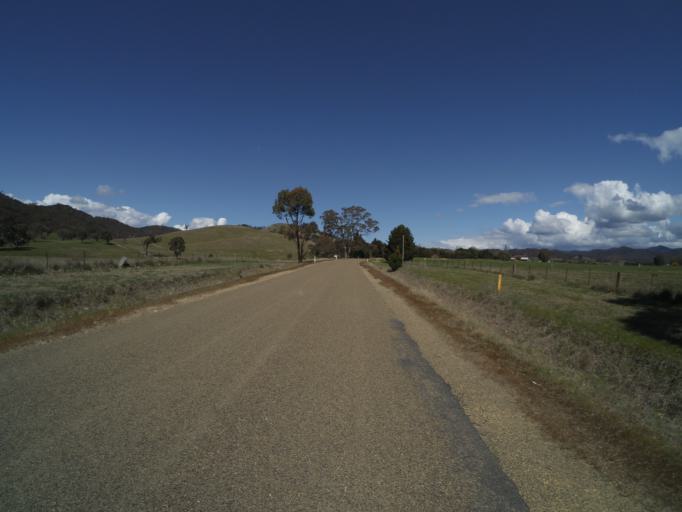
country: AU
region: Australian Capital Territory
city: Macquarie
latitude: -35.1491
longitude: 148.8834
